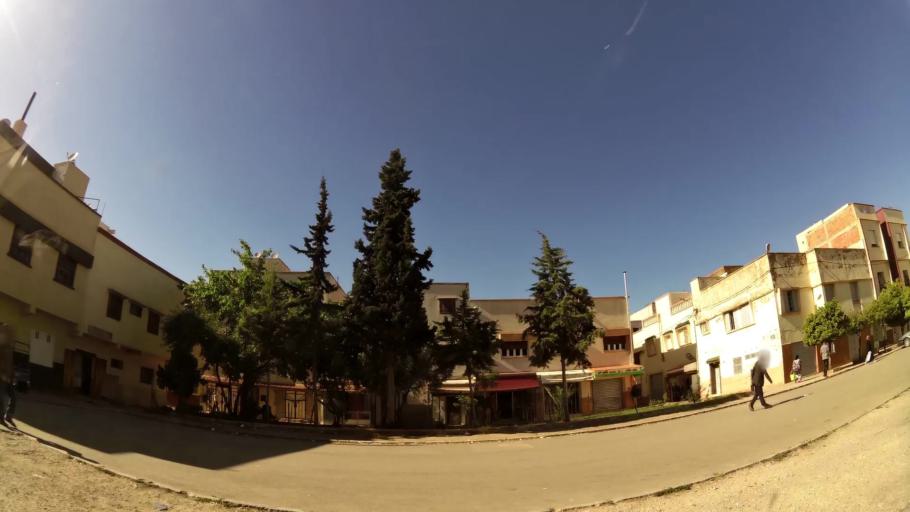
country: MA
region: Meknes-Tafilalet
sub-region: Meknes
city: Meknes
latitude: 33.8948
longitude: -5.5023
